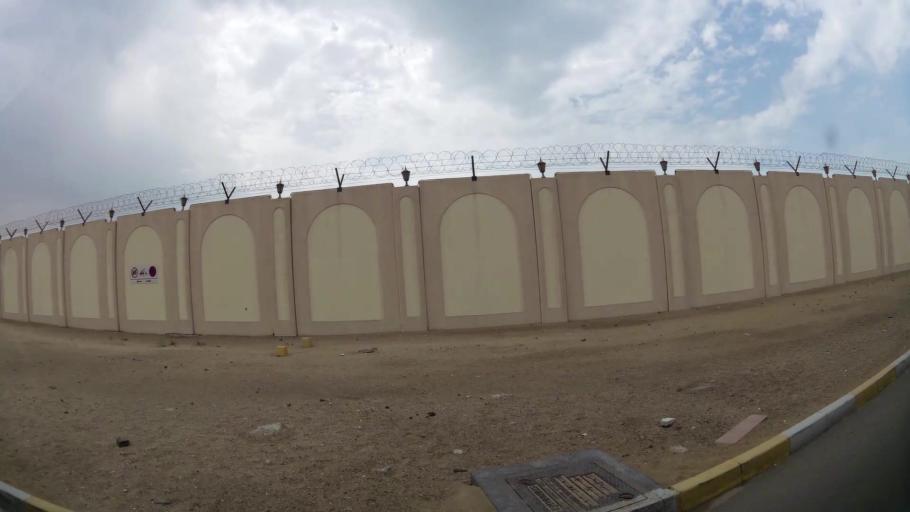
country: AE
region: Abu Dhabi
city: Abu Dhabi
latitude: 24.4330
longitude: 54.4544
